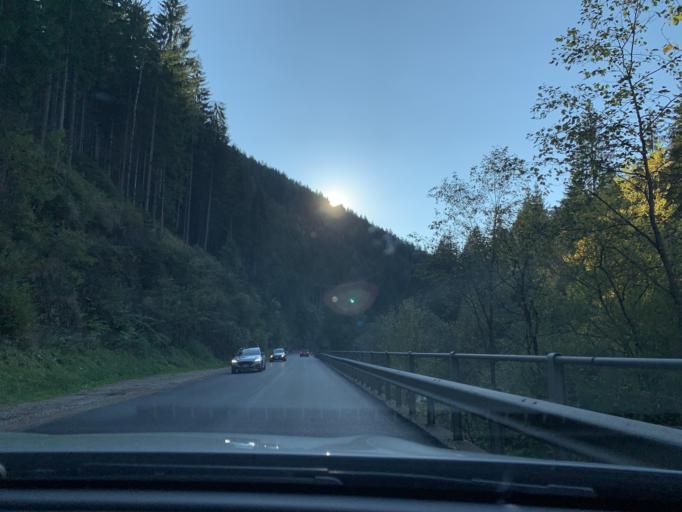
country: IT
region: Trentino-Alto Adige
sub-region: Bolzano
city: Nova Levante
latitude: 46.4262
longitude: 11.5193
